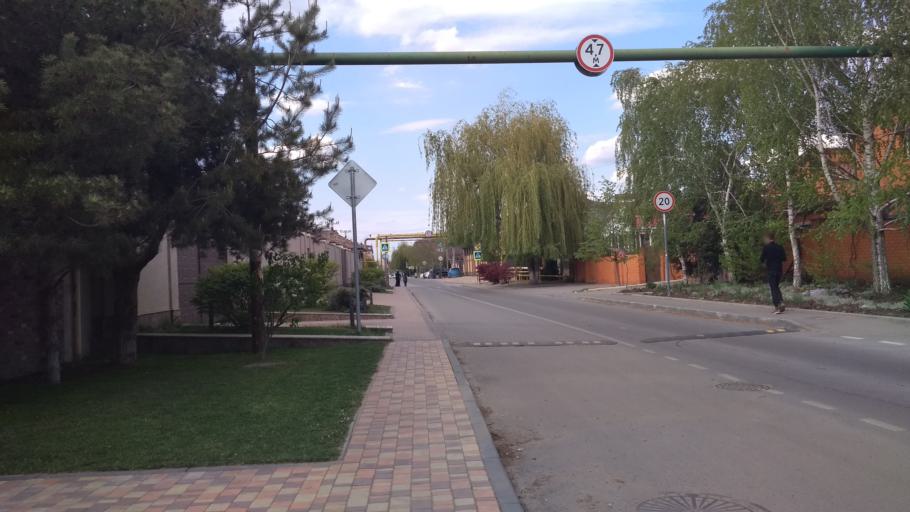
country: RU
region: Krasnodarskiy
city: Krasnodar
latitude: 45.0765
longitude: 39.0047
